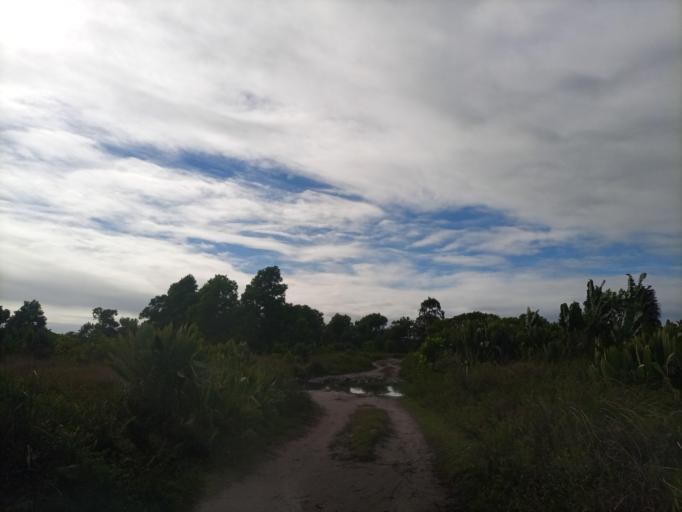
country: MG
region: Anosy
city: Fort Dauphin
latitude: -24.7791
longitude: 47.1868
